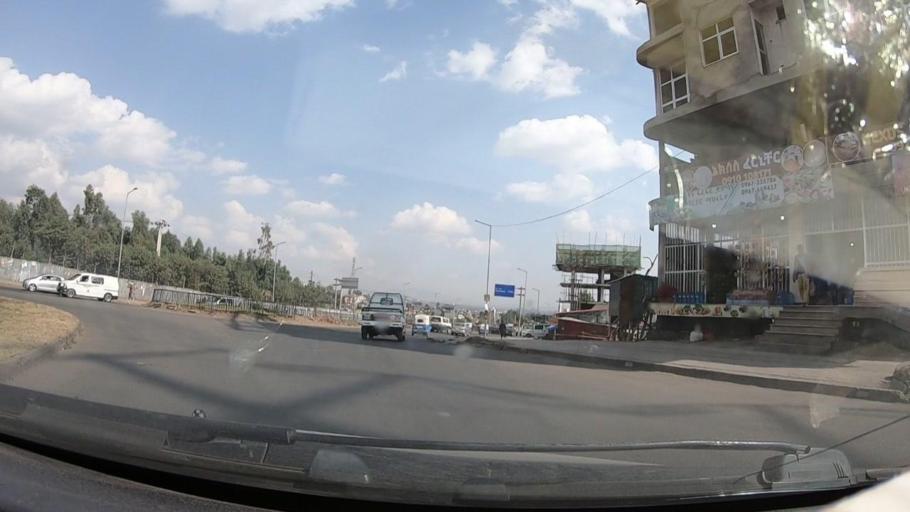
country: ET
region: Adis Abeba
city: Addis Ababa
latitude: 8.9915
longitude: 38.6890
